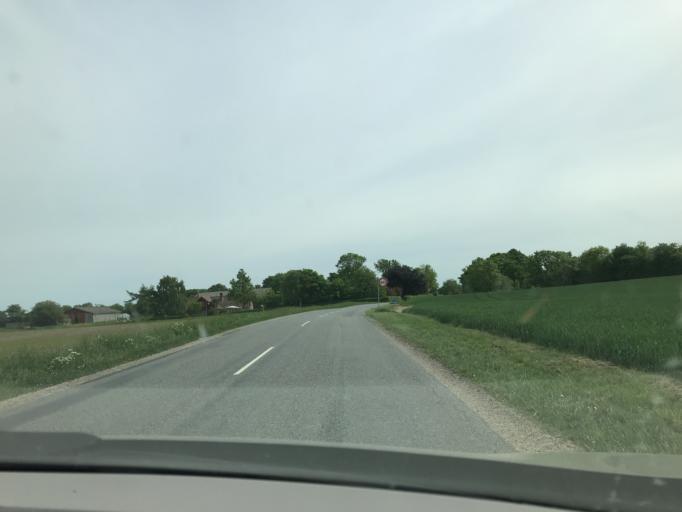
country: DK
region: Central Jutland
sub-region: Norddjurs Kommune
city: Allingabro
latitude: 56.5318
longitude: 10.3104
